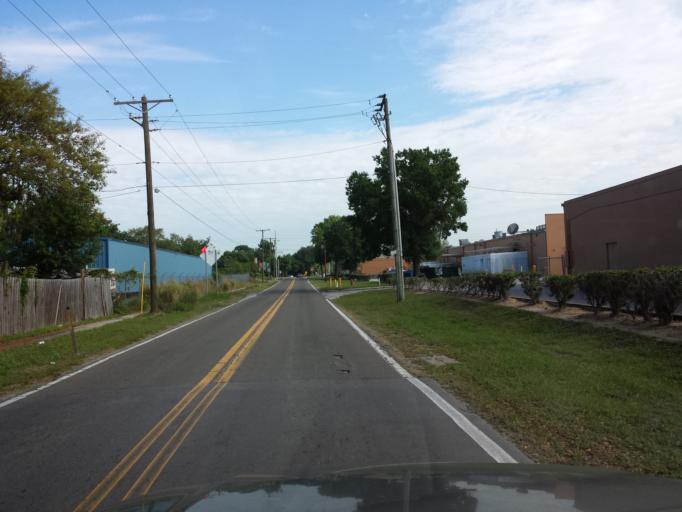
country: US
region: Florida
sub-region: Hillsborough County
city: Thonotosassa
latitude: 28.0523
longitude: -82.3354
